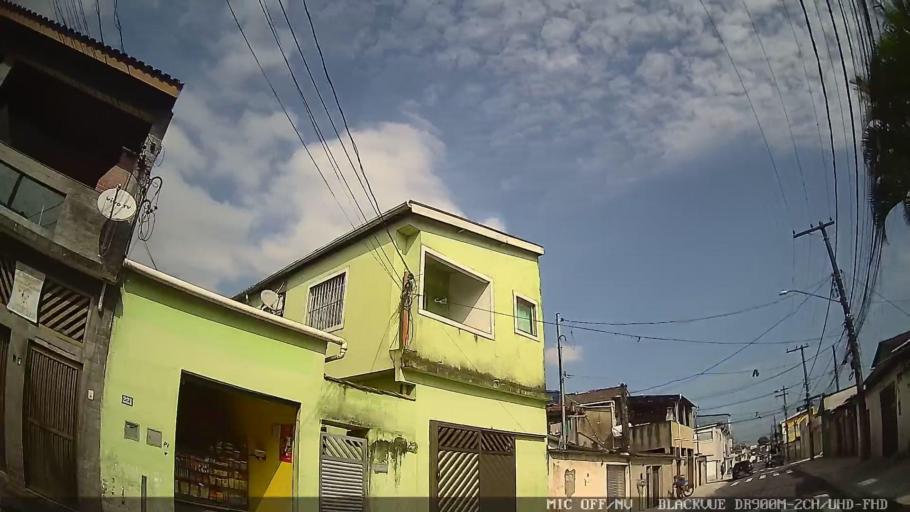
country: BR
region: Sao Paulo
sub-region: Santos
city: Santos
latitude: -23.9509
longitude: -46.2967
